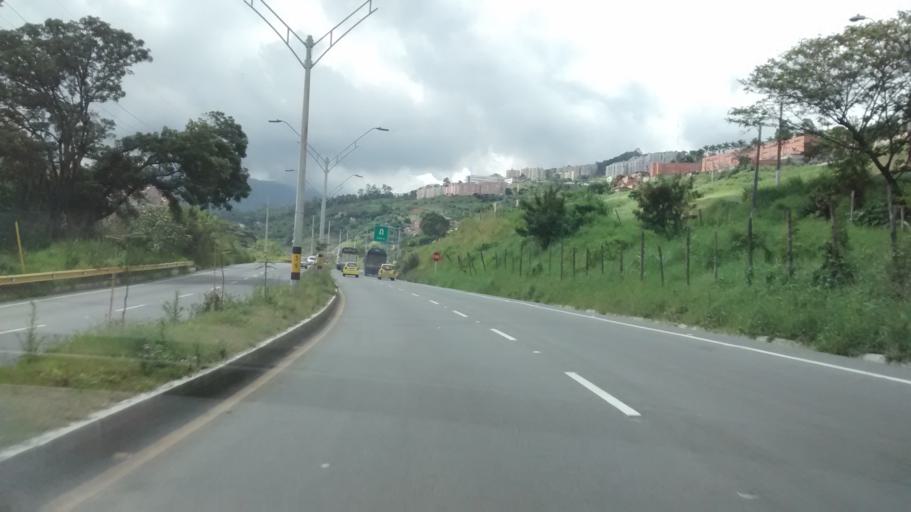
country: CO
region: Antioquia
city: Medellin
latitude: 6.2750
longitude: -75.5995
